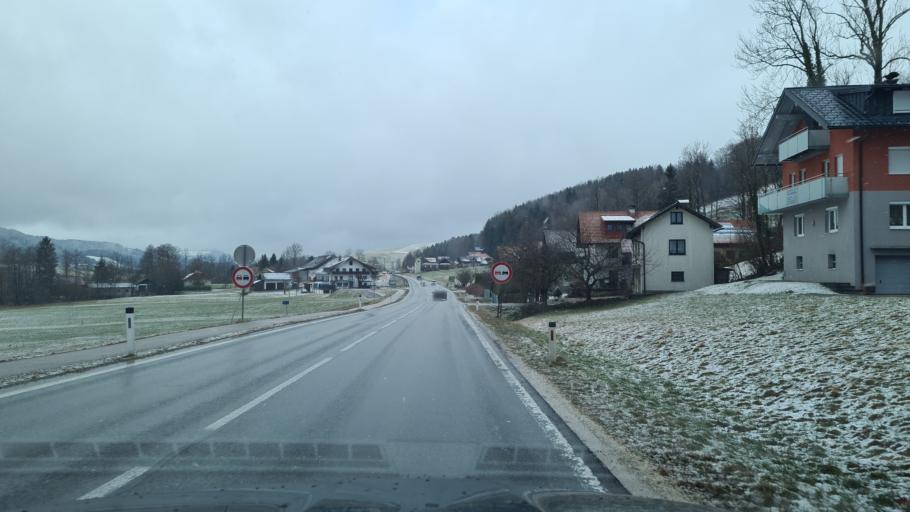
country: AT
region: Upper Austria
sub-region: Politischer Bezirk Vocklabruck
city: Zell am Moos
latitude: 47.8823
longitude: 13.3196
